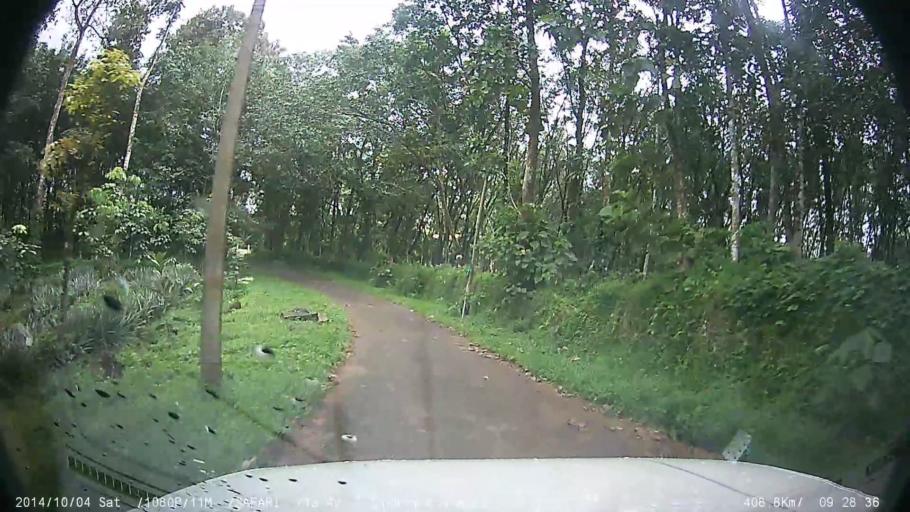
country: IN
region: Kerala
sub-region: Kottayam
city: Palackattumala
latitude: 9.7875
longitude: 76.5718
